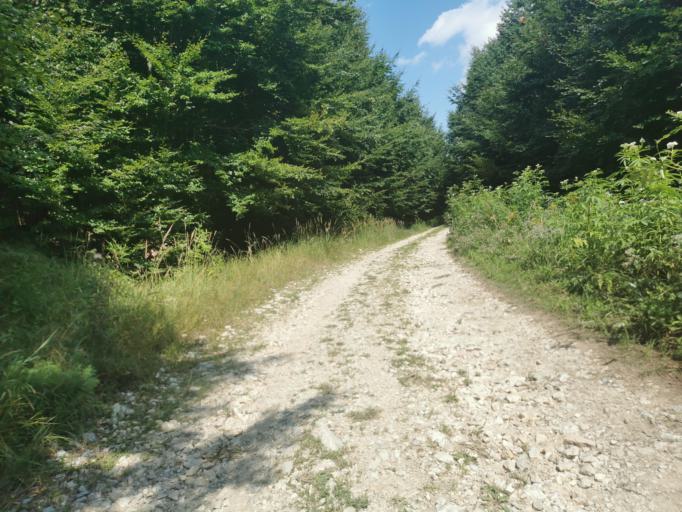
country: SK
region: Trenciansky
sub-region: Okres Myjava
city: Myjava
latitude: 48.8204
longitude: 17.5763
